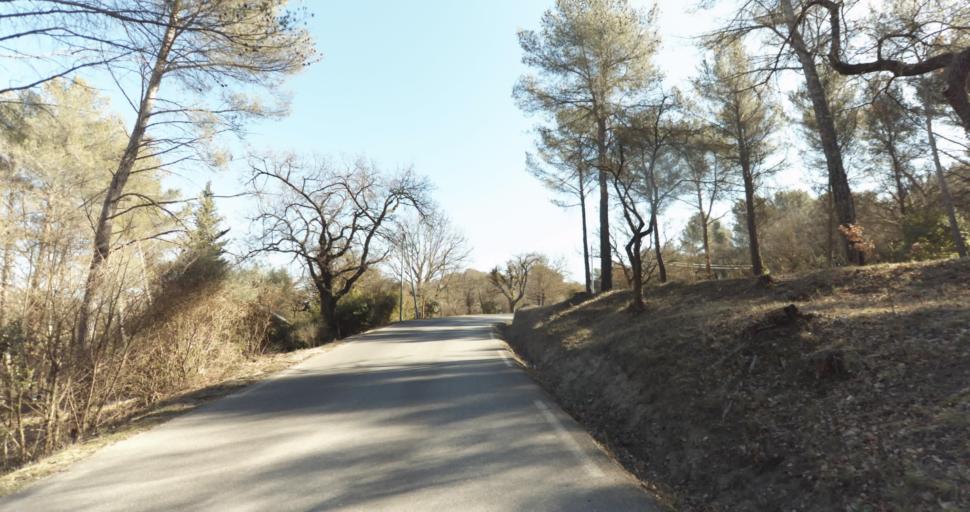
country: FR
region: Provence-Alpes-Cote d'Azur
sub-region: Departement des Bouches-du-Rhone
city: Peypin
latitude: 43.3935
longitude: 5.5702
